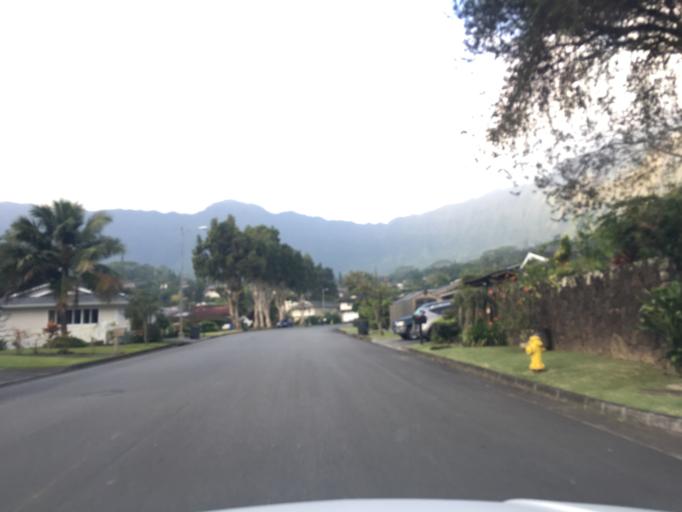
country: US
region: Hawaii
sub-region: Honolulu County
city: Maunawili
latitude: 21.3613
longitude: -157.7659
